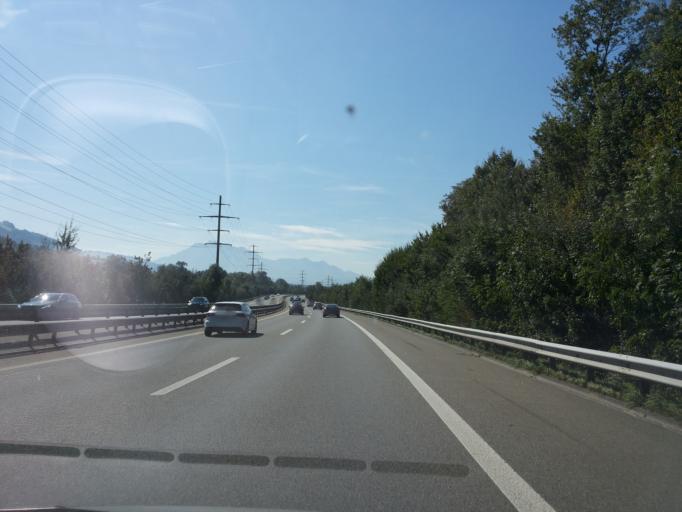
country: CH
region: Aargau
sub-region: Bezirk Muri
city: Oberruti
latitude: 47.1426
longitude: 8.4109
